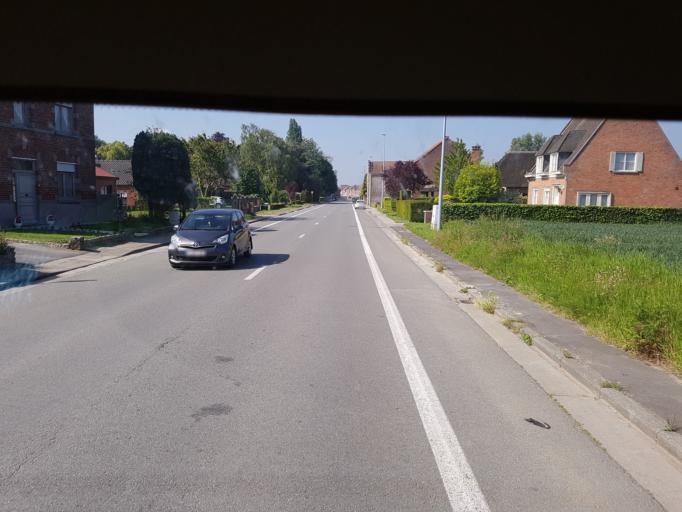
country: FR
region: Nord-Pas-de-Calais
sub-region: Departement du Nord
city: Deulemont
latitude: 50.7483
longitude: 2.9397
